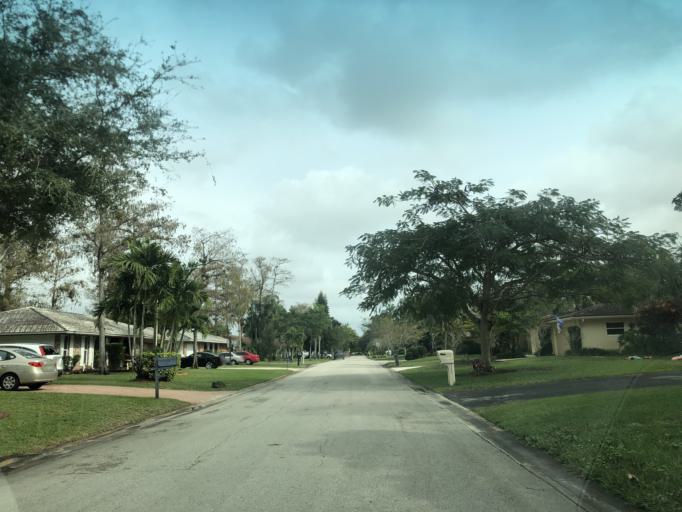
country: US
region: Florida
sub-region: Broward County
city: Margate
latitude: 26.2482
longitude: -80.2382
